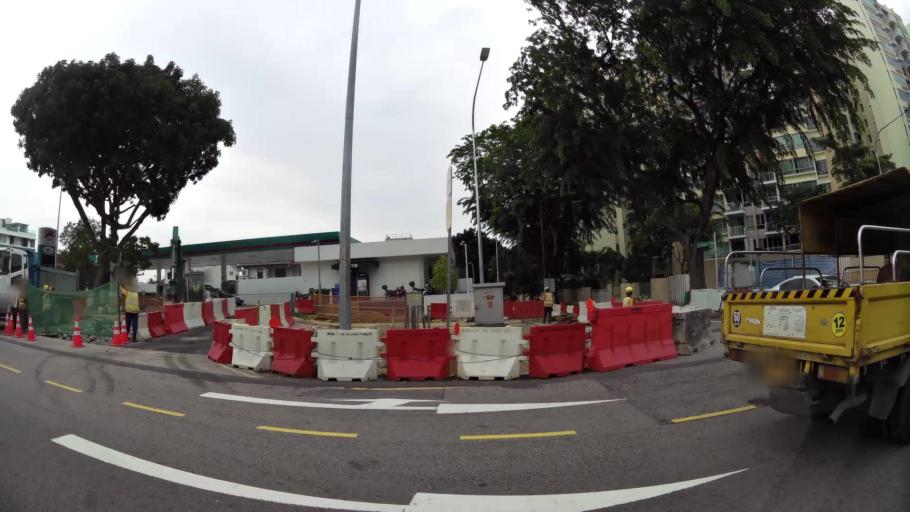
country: SG
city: Singapore
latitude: 1.3584
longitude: 103.8832
